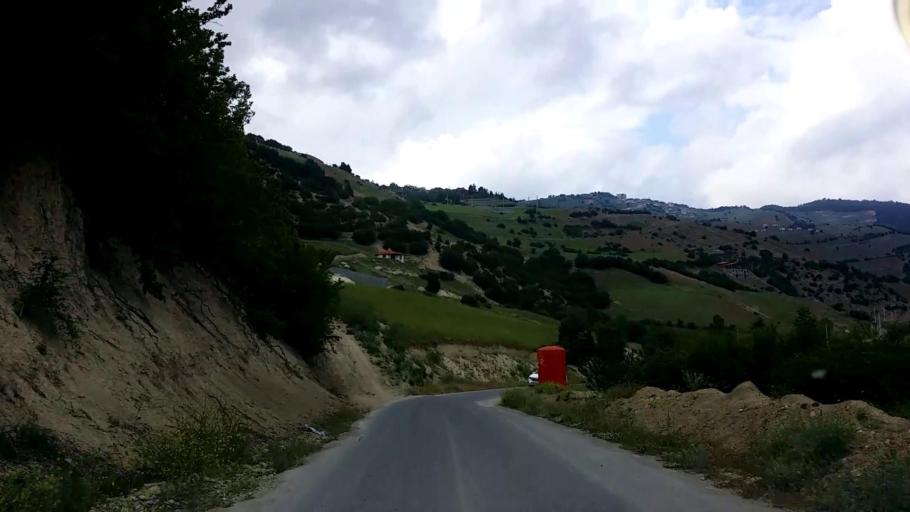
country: IR
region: Mazandaran
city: Chalus
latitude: 36.5424
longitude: 51.2724
